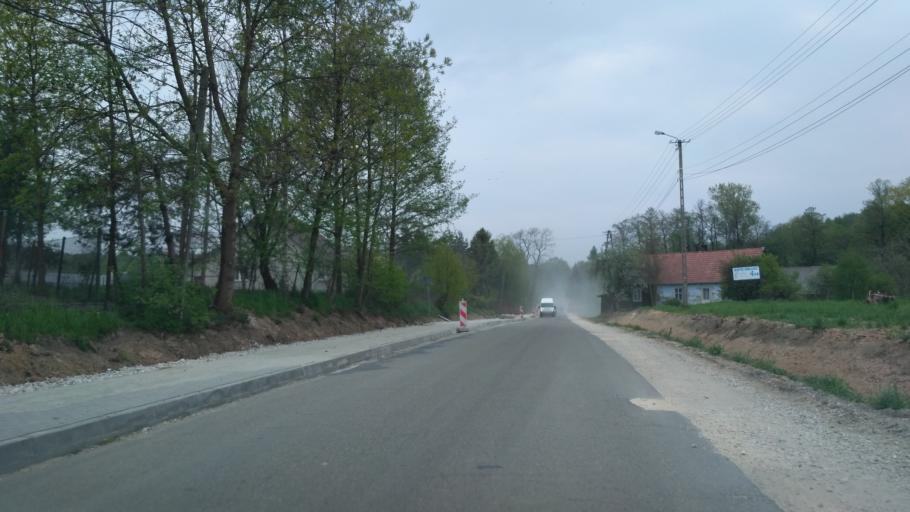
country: PL
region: Lesser Poland Voivodeship
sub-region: Powiat tarnowski
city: Skrzyszow
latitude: 49.9807
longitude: 21.0649
